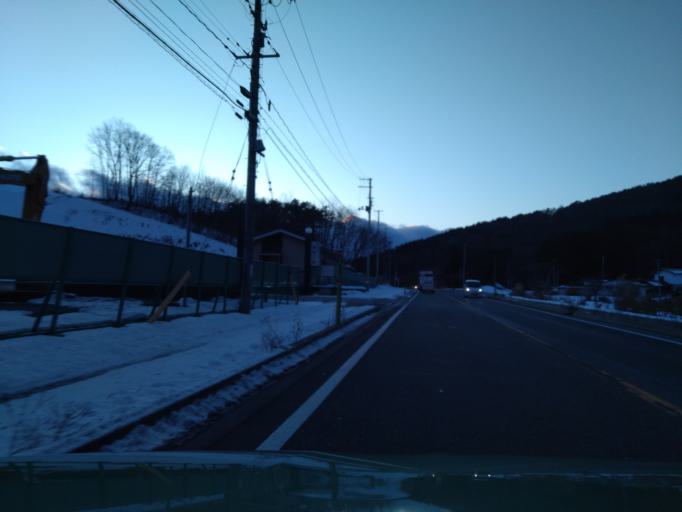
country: JP
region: Iwate
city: Shizukuishi
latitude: 39.6915
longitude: 141.0073
